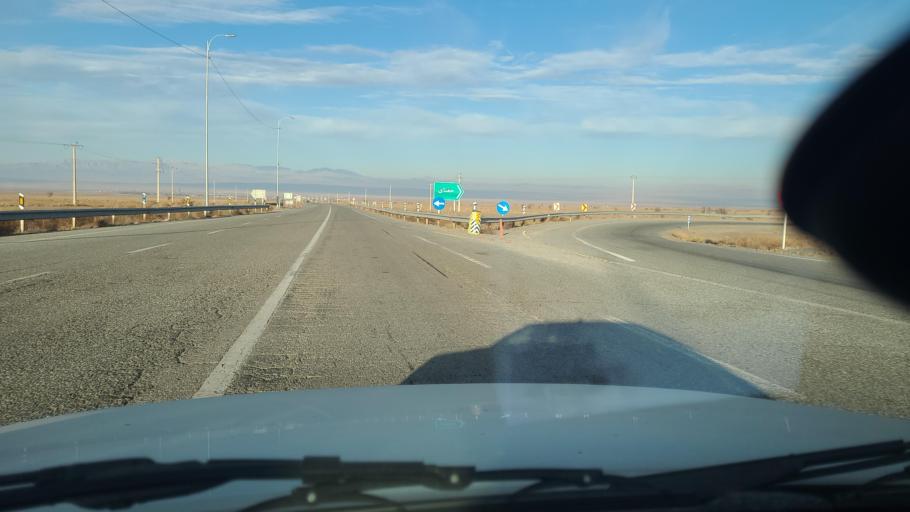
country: IR
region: Razavi Khorasan
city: Neqab
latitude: 36.5134
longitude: 57.5409
